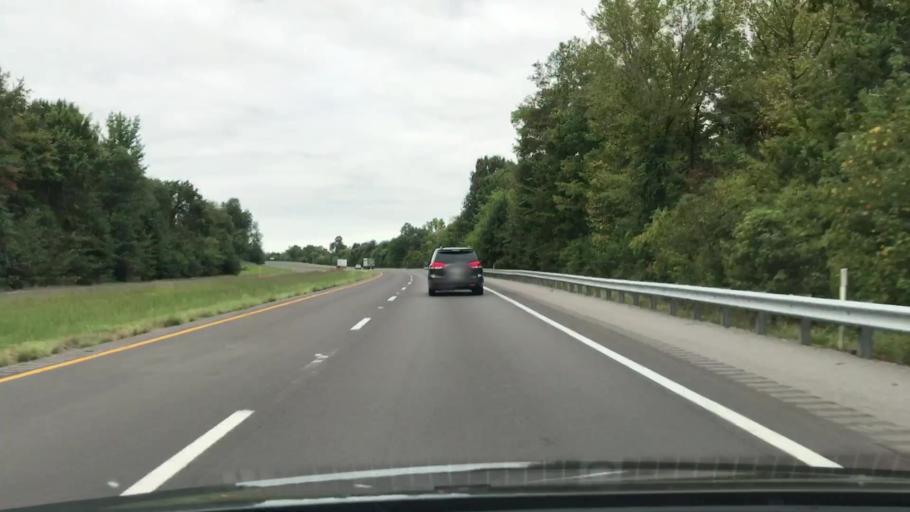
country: US
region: Kentucky
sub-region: Fulton County
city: Fulton
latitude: 36.5866
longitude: -88.8195
